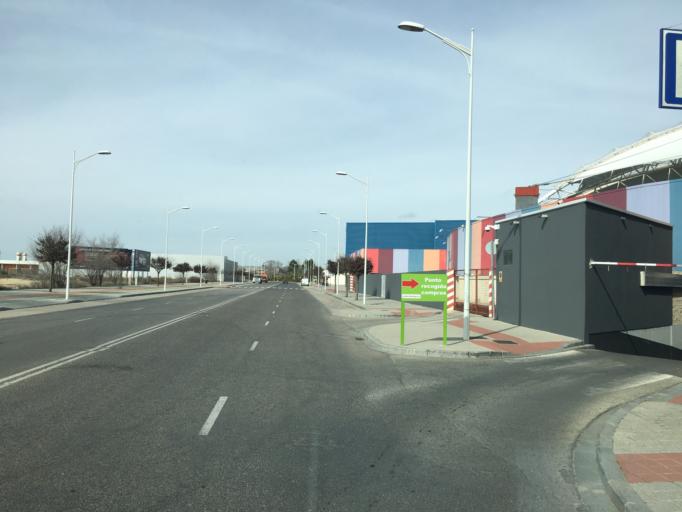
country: ES
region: Castille-La Mancha
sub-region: Provincia de Albacete
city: Albacete
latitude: 39.0070
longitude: -1.8797
